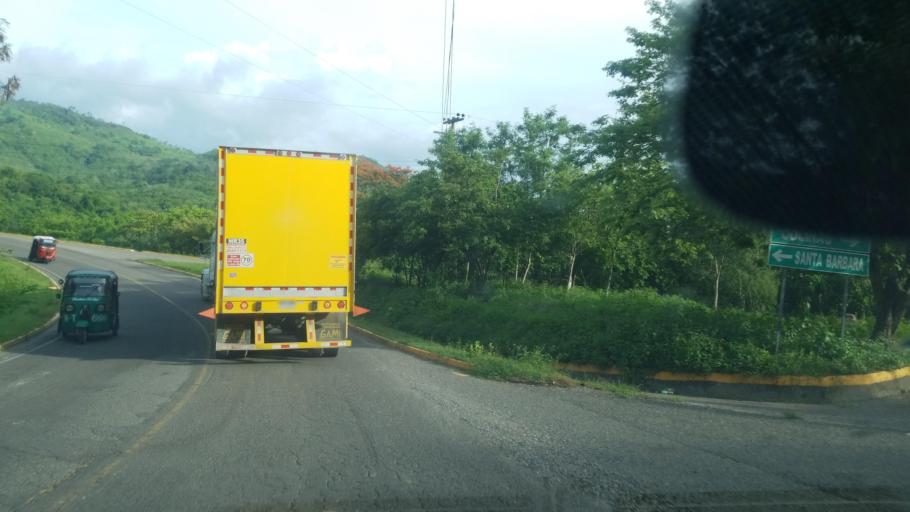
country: HN
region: Santa Barbara
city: Ilama
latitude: 15.0672
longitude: -88.2303
